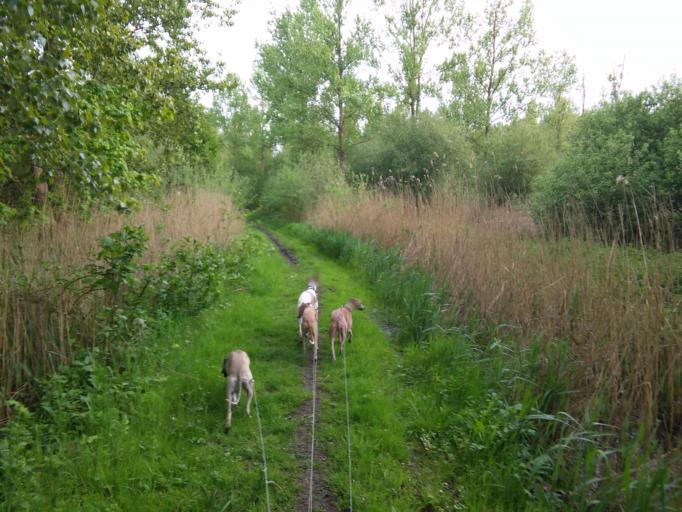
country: BE
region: Flanders
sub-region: Provincie Antwerpen
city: Rumst
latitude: 51.0453
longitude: 4.4293
